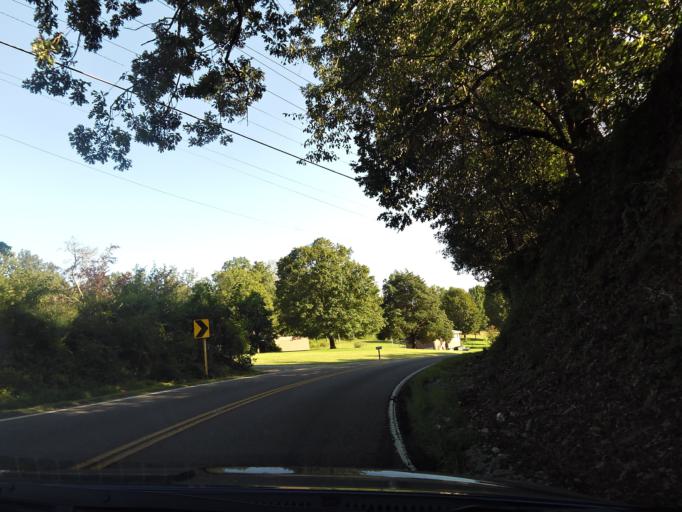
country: US
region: Tennessee
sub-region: Union County
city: Condon
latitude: 36.1866
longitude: -83.8119
